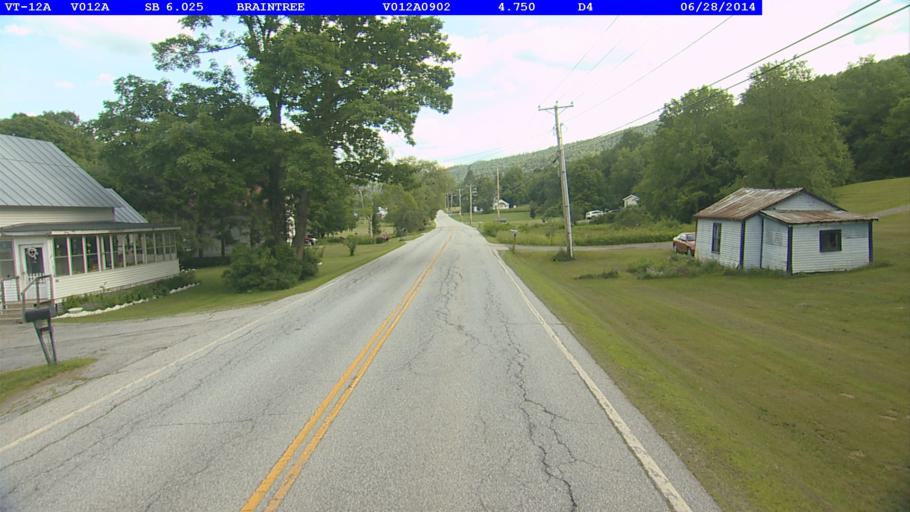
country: US
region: Vermont
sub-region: Orange County
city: Randolph
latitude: 43.9760
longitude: -72.7494
